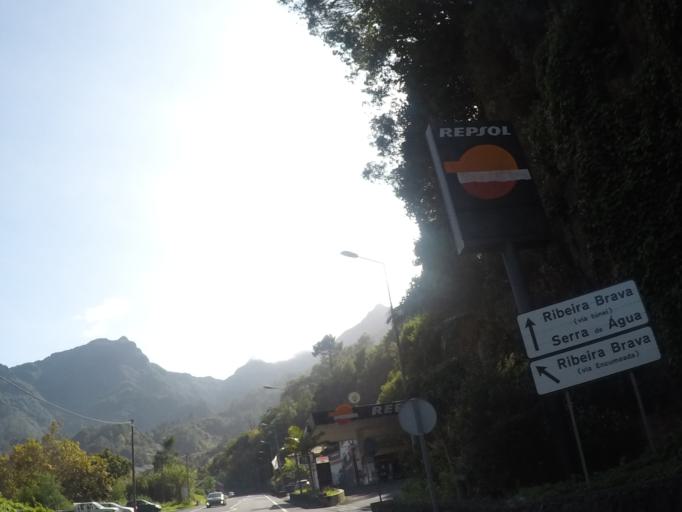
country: PT
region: Madeira
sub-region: Sao Vicente
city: Sao Vicente
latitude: 32.7797
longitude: -17.0342
